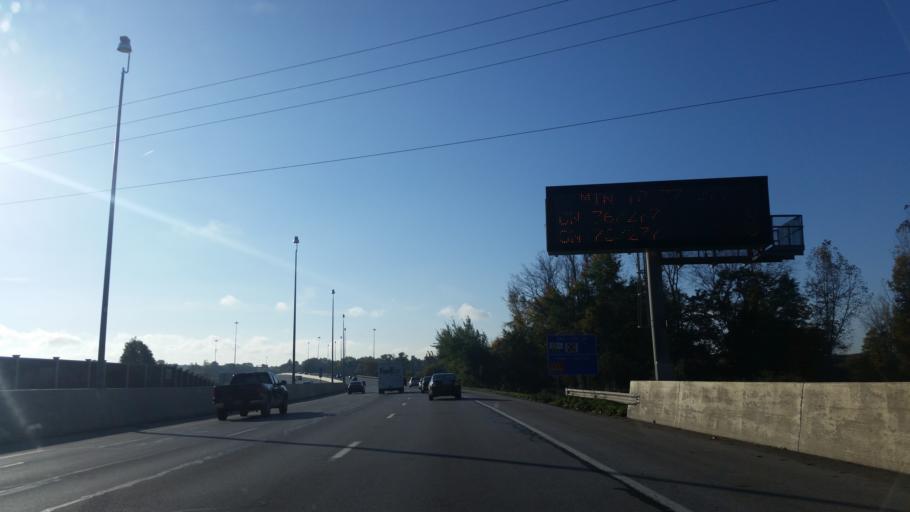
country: US
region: Ohio
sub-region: Summit County
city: Fairlawn
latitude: 41.0885
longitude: -81.5834
